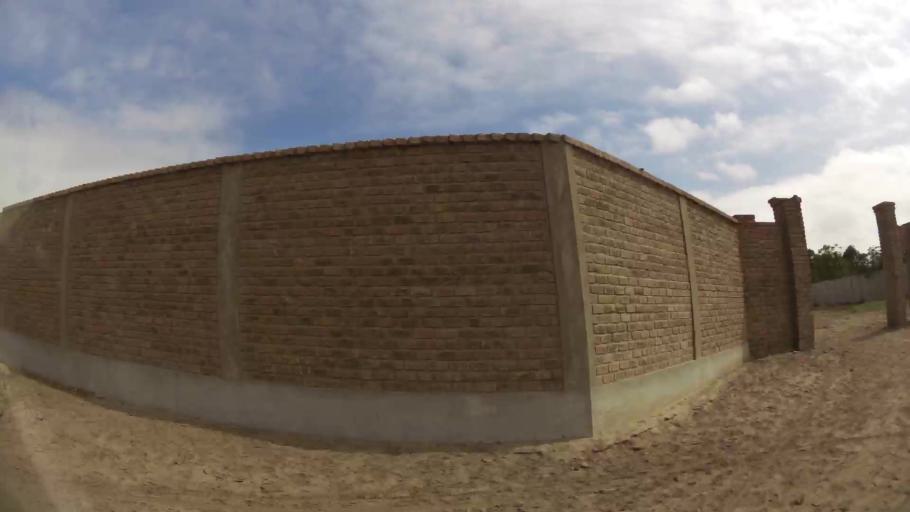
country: PE
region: Lima
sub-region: Provincia de Canete
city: Mala
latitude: -12.7306
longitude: -76.6214
